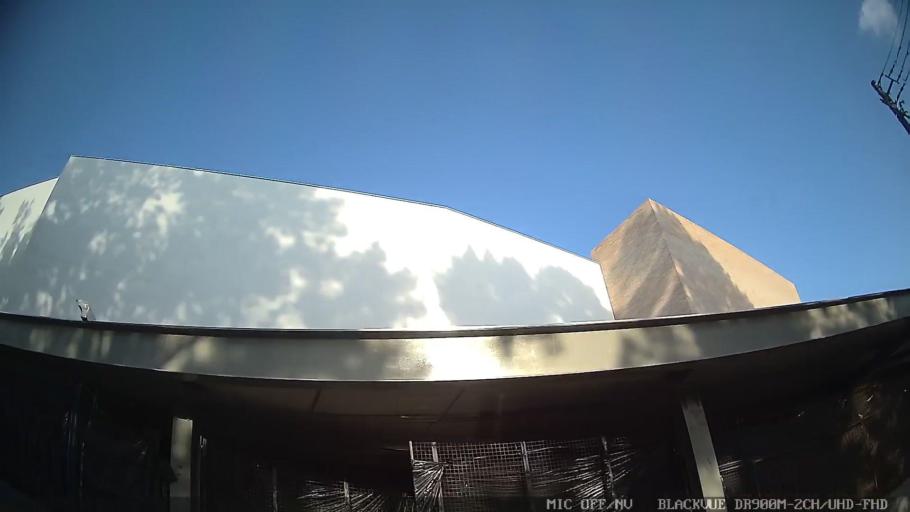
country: BR
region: Sao Paulo
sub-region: Taboao Da Serra
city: Taboao da Serra
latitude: -23.6361
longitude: -46.7697
